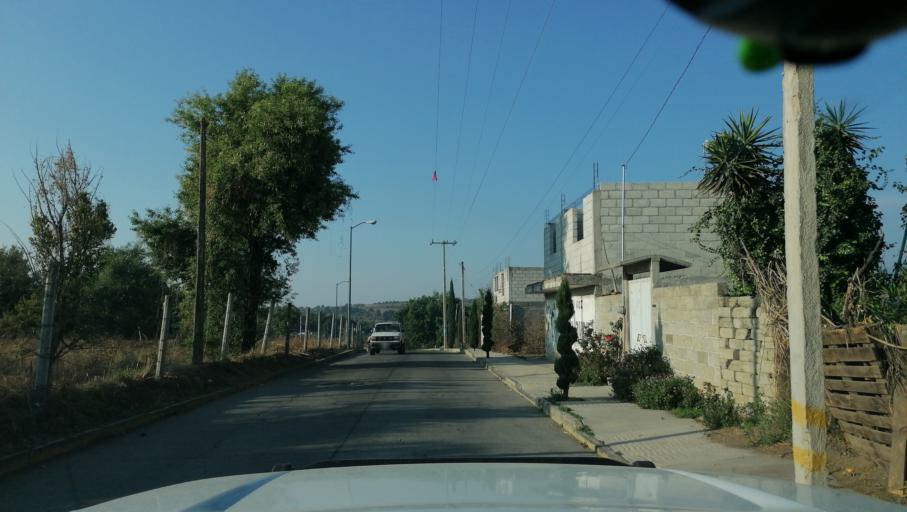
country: MX
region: Puebla
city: San Andres Calpan
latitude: 19.1065
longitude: -98.4401
